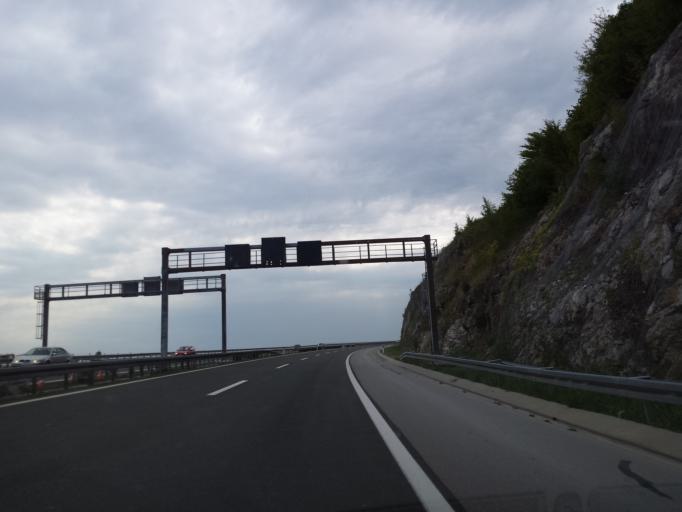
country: HR
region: Karlovacka
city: Ostarije
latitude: 45.1772
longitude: 15.2770
